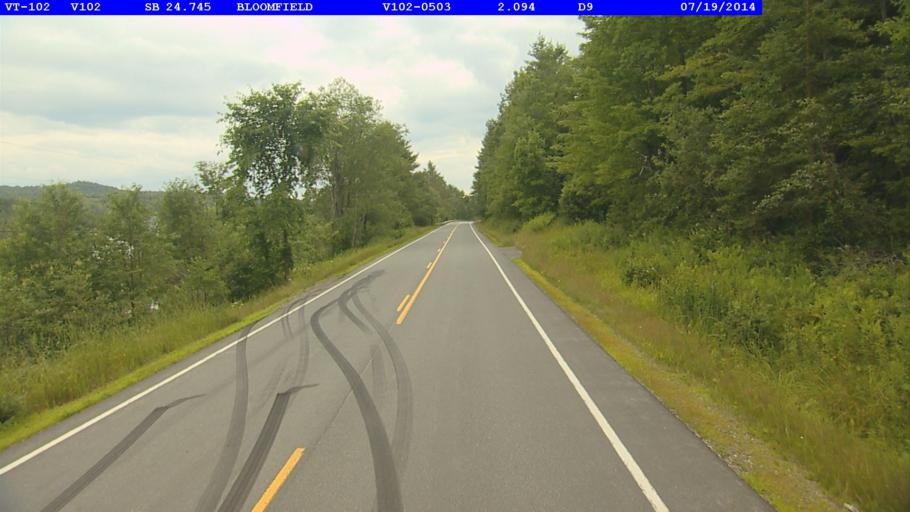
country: US
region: New Hampshire
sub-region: Coos County
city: Stratford
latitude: 44.7697
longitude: -71.6059
